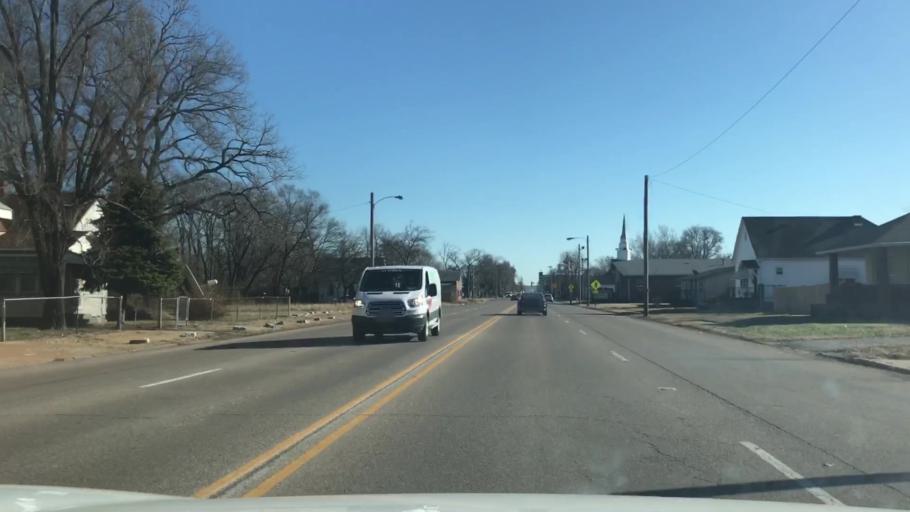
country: US
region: Illinois
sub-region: Saint Clair County
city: East Saint Louis
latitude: 38.6080
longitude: -90.1375
